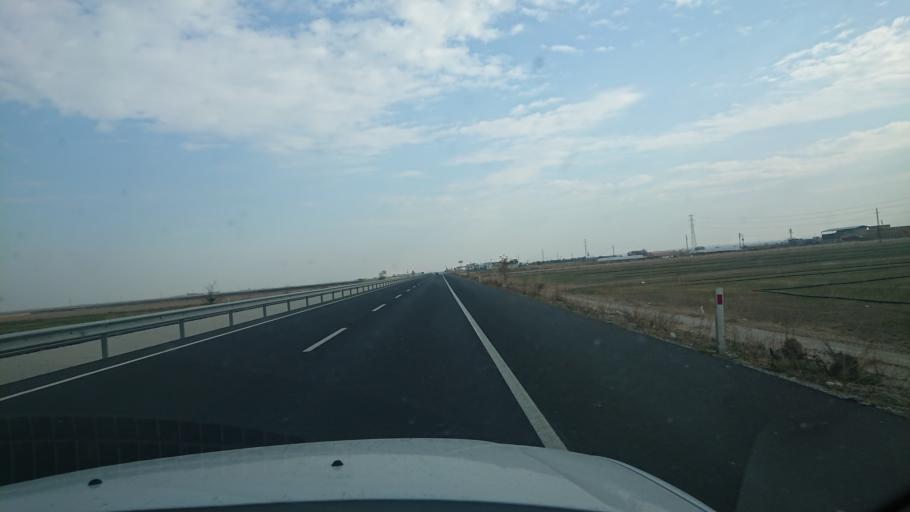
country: TR
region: Aksaray
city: Yesilova
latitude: 38.3003
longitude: 33.7966
